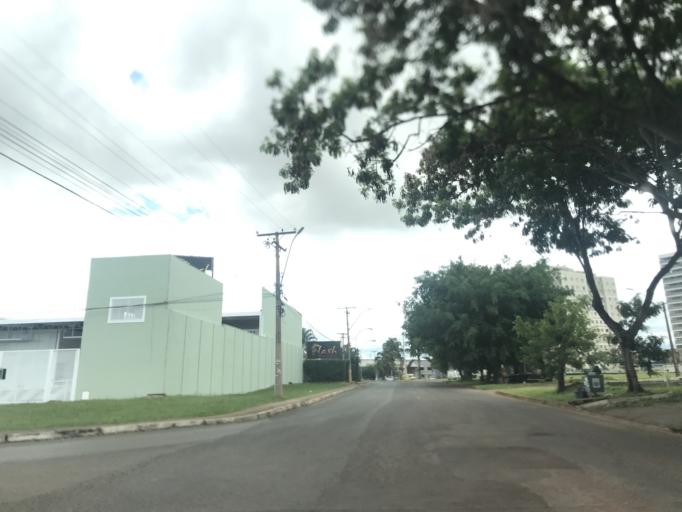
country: BR
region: Federal District
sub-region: Brasilia
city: Brasilia
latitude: -15.8734
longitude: -48.0339
